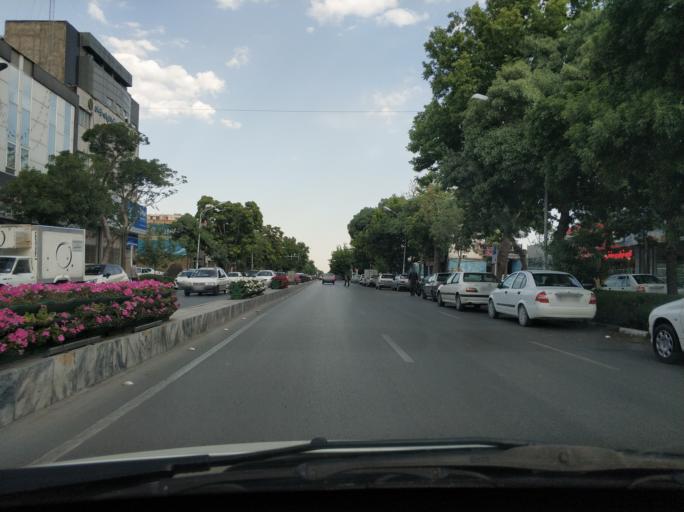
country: IR
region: Razavi Khorasan
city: Mashhad
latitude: 36.2807
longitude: 59.5964
